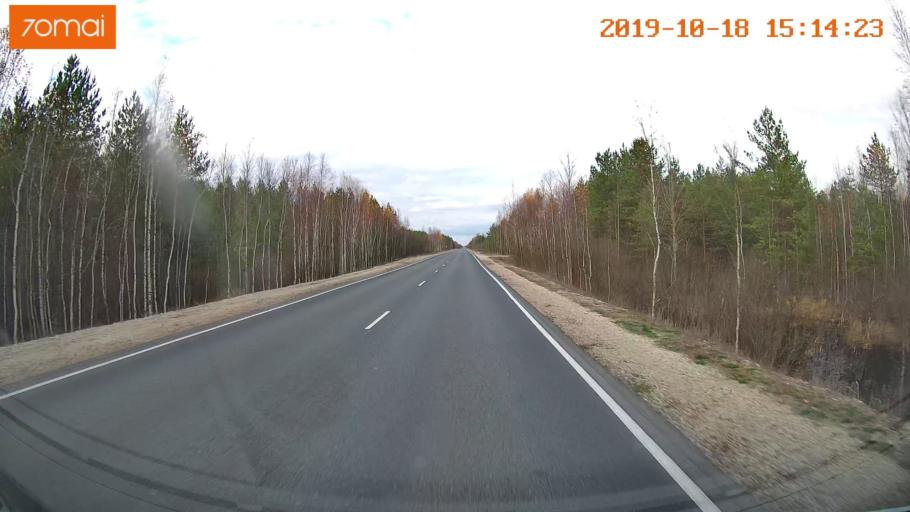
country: RU
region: Vladimir
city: Gus'-Khrustal'nyy
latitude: 55.6018
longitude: 40.7201
